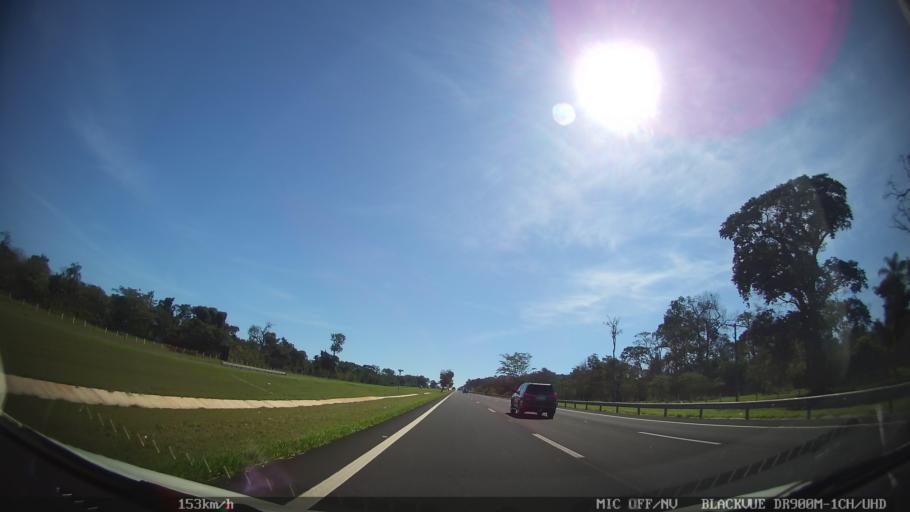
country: BR
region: Sao Paulo
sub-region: Santa Rita Do Passa Quatro
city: Santa Rita do Passa Quatro
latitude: -21.7250
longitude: -47.5869
